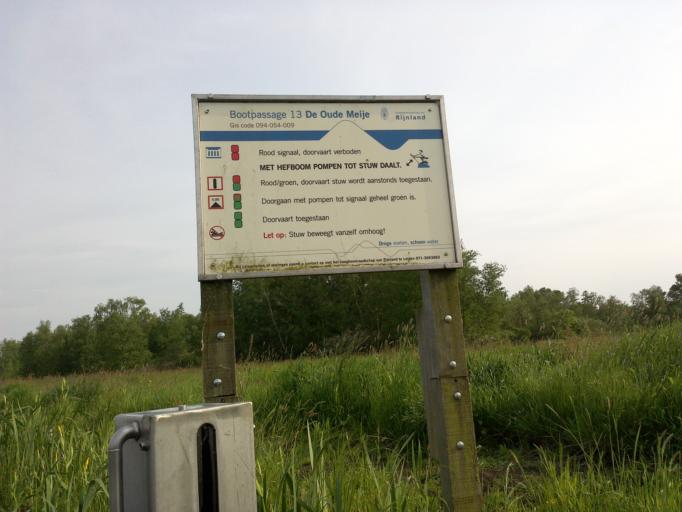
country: NL
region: South Holland
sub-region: Gemeente Nieuwkoop
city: Nieuwkoop
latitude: 52.1356
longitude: 4.7891
